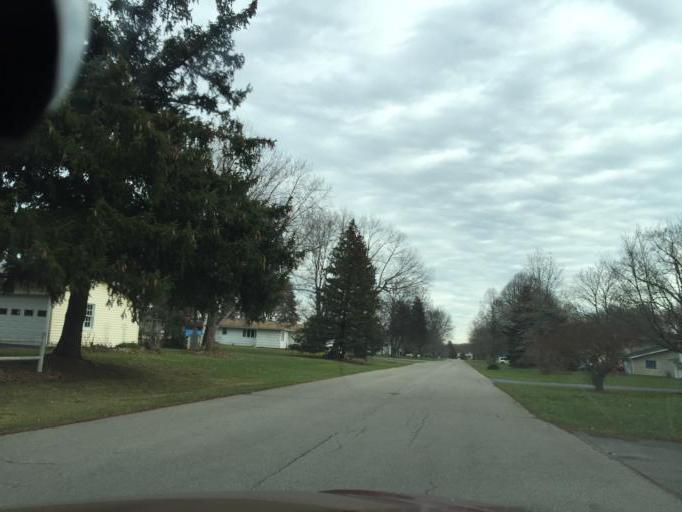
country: US
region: New York
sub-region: Monroe County
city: North Gates
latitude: 43.1137
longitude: -77.7237
